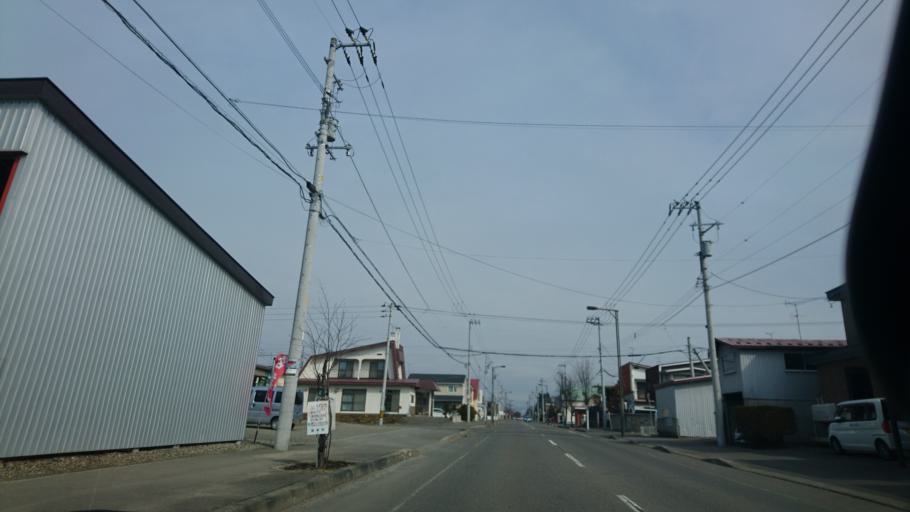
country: JP
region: Hokkaido
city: Otofuke
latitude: 42.9699
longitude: 143.2127
